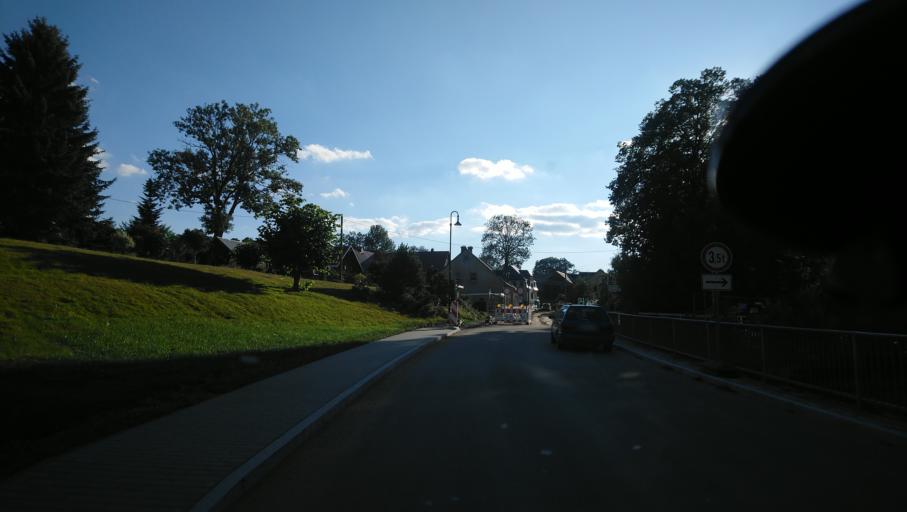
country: DE
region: Saxony
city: Schlettau
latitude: 50.5426
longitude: 12.9586
